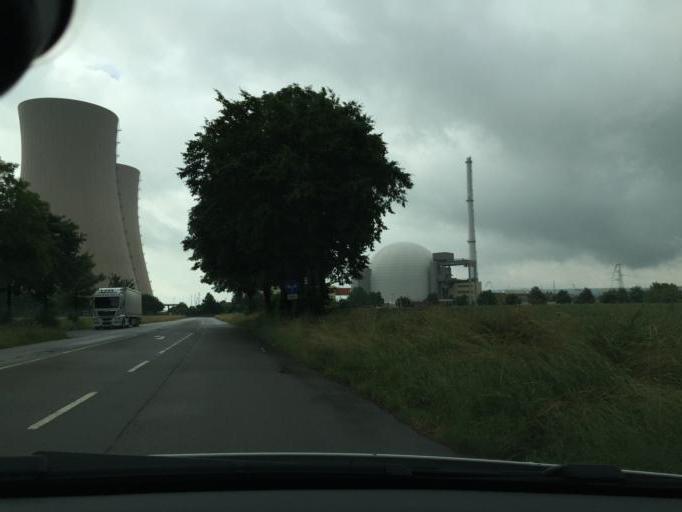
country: DE
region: Lower Saxony
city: Hehlen
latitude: 52.0393
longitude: 9.4082
